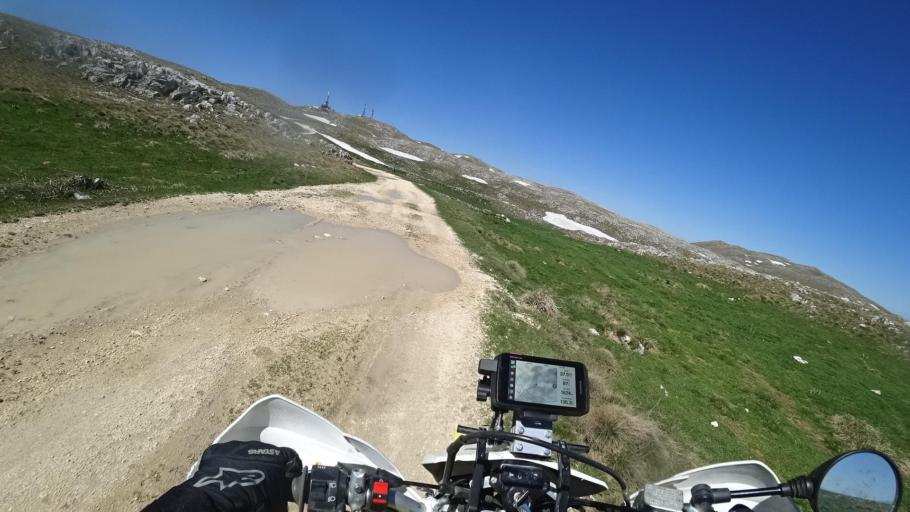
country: BA
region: Federation of Bosnia and Herzegovina
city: Travnik
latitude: 44.2802
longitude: 17.6369
